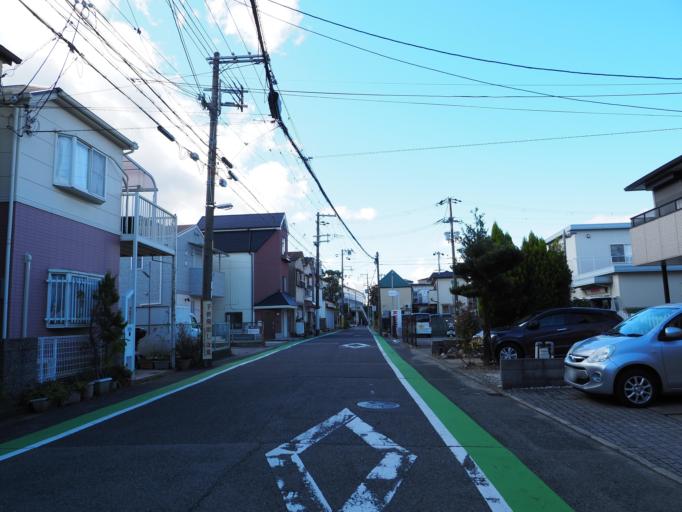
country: JP
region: Hyogo
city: Ashiya
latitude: 34.7322
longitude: 135.3196
